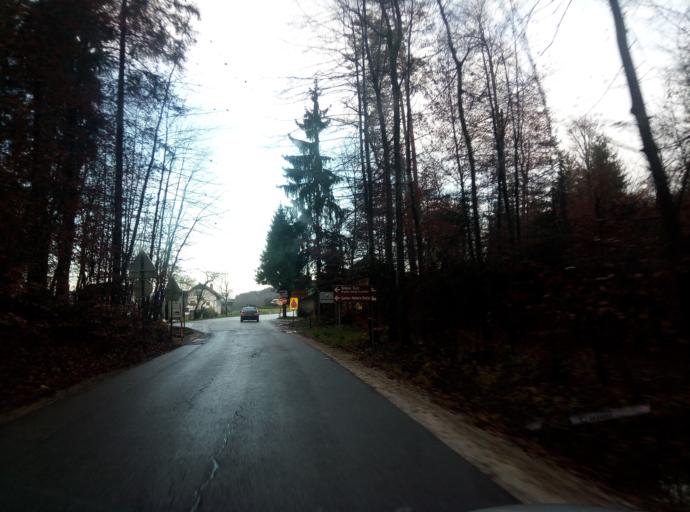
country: SI
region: Komenda
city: Moste
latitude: 46.1680
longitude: 14.5391
